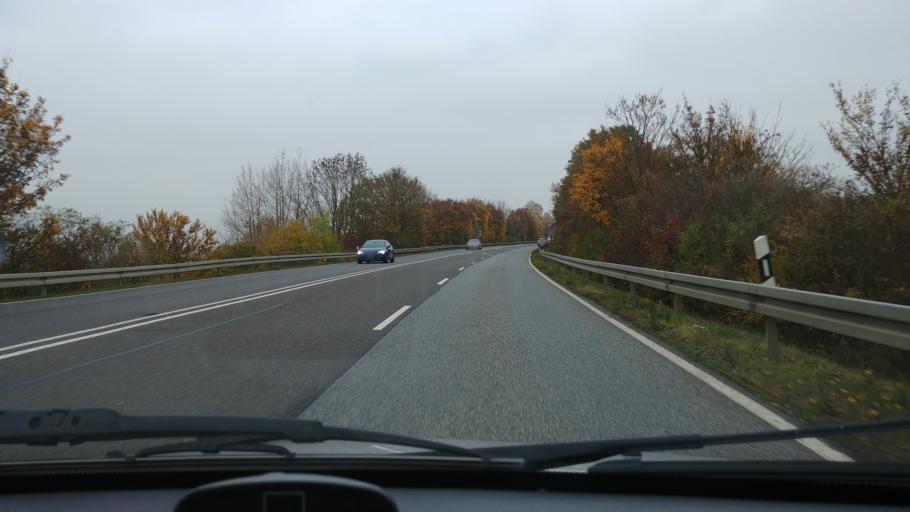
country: DE
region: Hesse
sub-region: Regierungsbezirk Giessen
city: Elz
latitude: 50.4689
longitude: 8.0564
